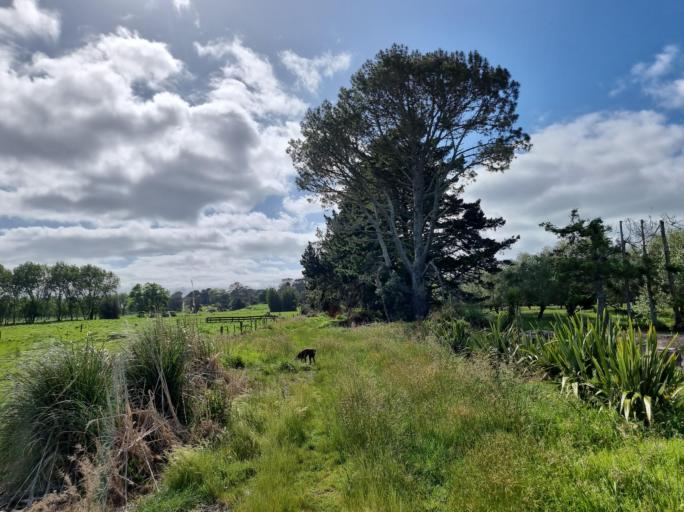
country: NZ
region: Auckland
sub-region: Auckland
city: Wellsford
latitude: -36.1256
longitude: 174.5873
